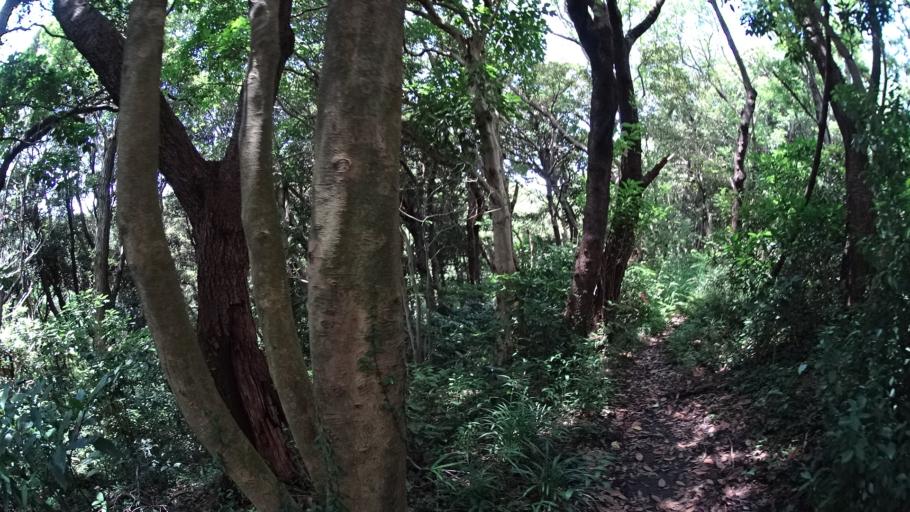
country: JP
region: Kanagawa
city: Yokosuka
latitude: 35.2137
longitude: 139.6701
